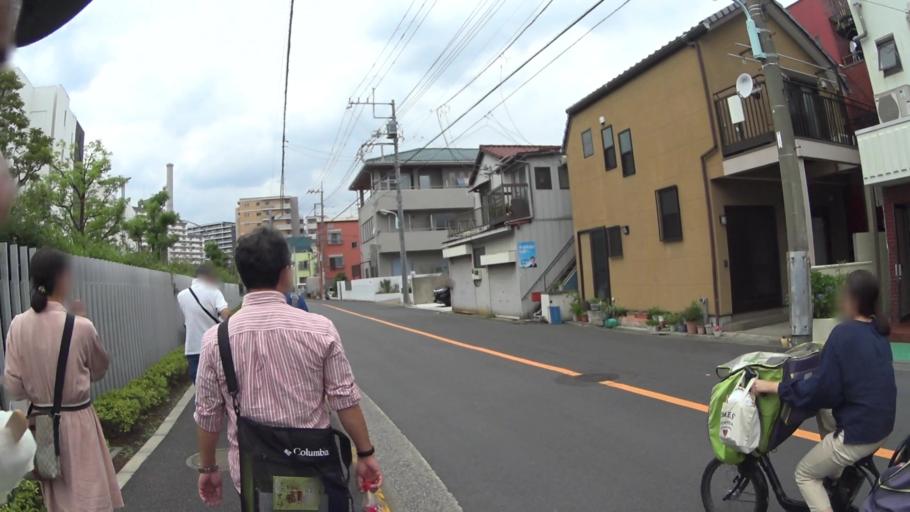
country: JP
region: Tokyo
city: Urayasu
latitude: 35.7128
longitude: 139.8379
